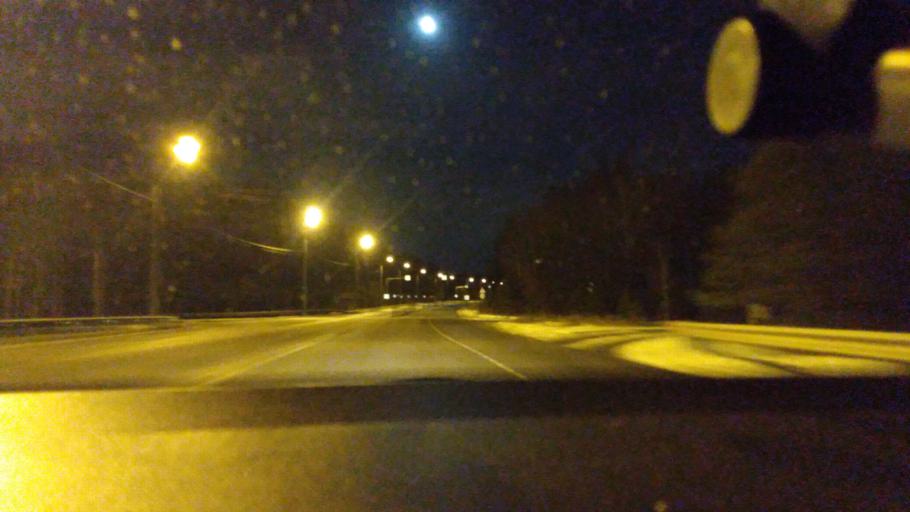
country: RU
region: Moskovskaya
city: Il'inskiy Pogost
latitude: 55.4869
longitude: 38.9148
